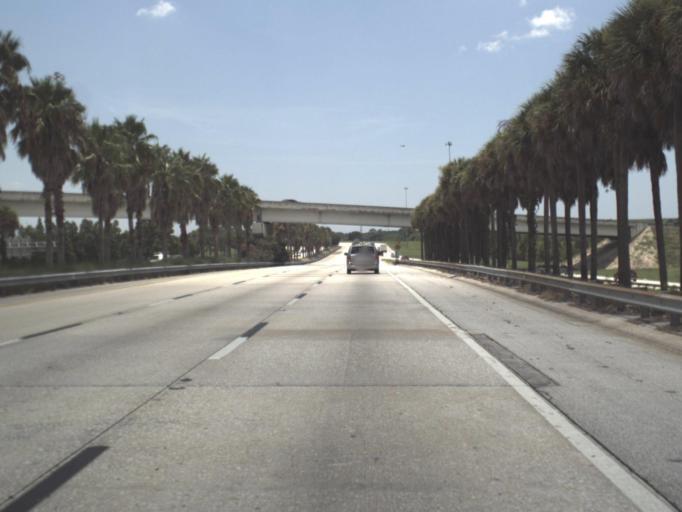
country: US
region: Florida
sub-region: Pinellas County
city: Feather Sound
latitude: 27.8783
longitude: -82.6596
